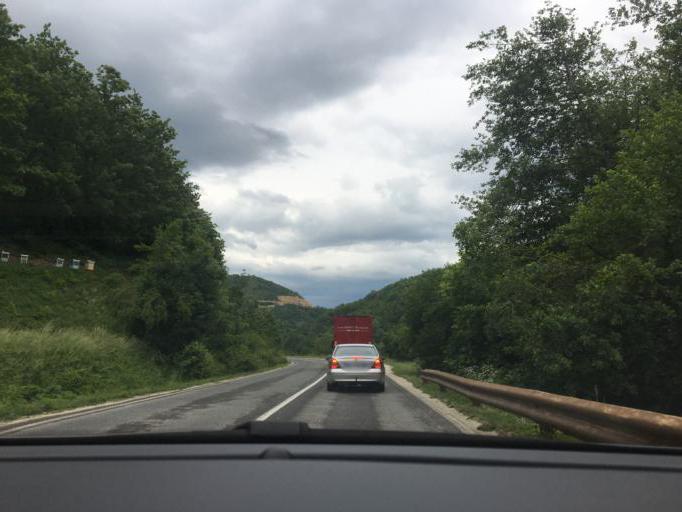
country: MK
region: Drugovo
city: Drugovo
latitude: 41.4794
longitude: 20.8862
